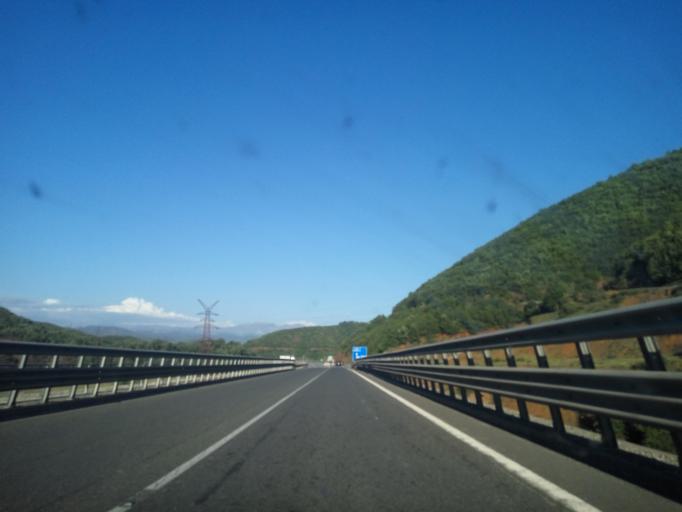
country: AL
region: Lezhe
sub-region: Rrethi i Mirdites
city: Rreshen
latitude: 41.7811
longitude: 19.8448
